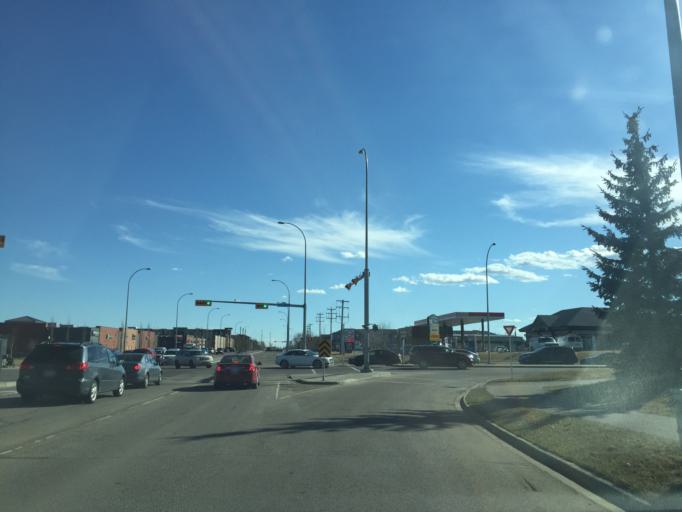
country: CA
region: Alberta
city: Airdrie
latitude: 51.2932
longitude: -114.0254
